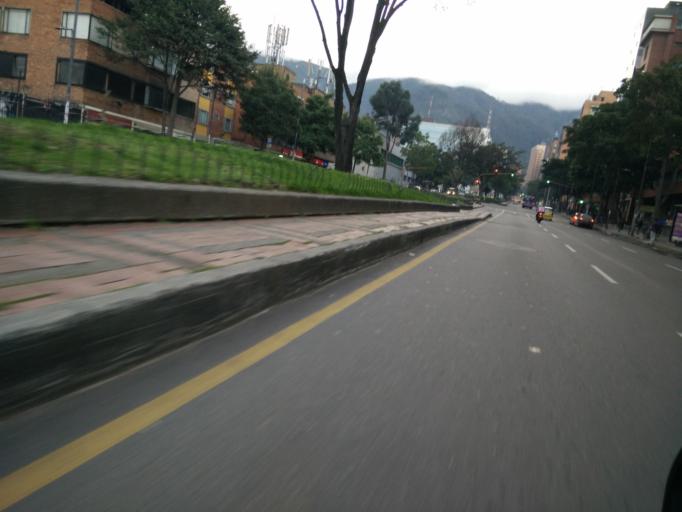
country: CO
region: Bogota D.C.
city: Barrio San Luis
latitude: 4.6589
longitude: -74.0614
